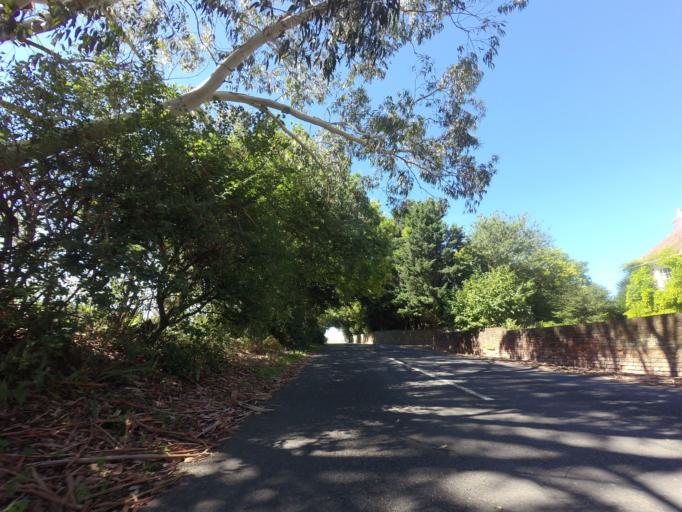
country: GB
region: England
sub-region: Kent
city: Westgate on Sea
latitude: 51.3304
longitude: 1.3458
